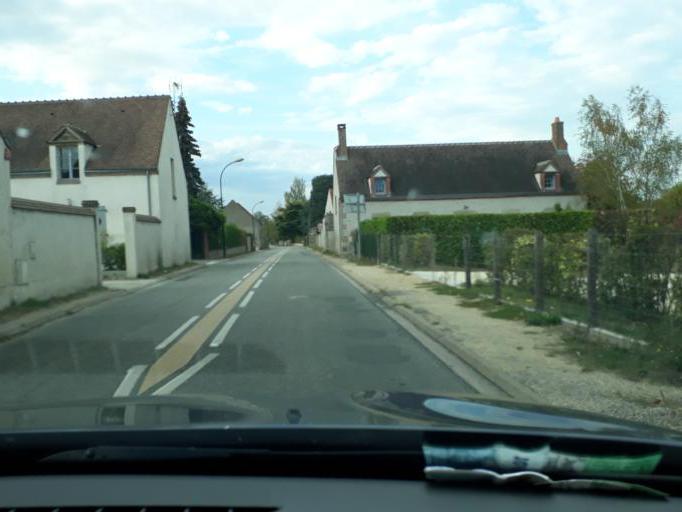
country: FR
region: Centre
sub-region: Departement du Loiret
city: Saint-Benoit-sur-Loire
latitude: 47.8126
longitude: 2.3032
